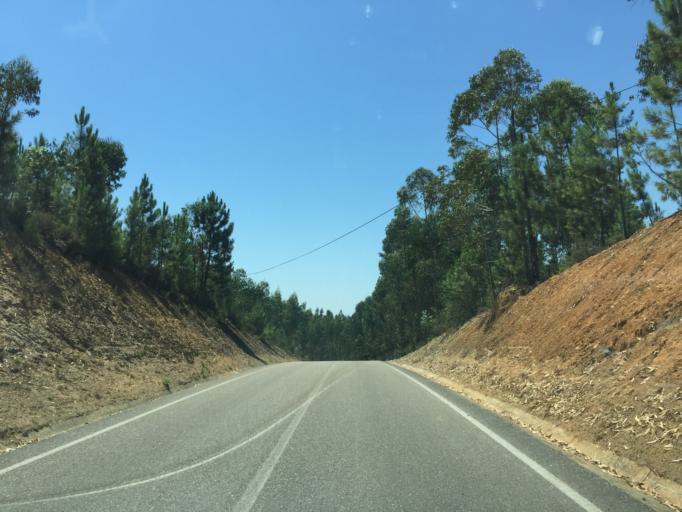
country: PT
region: Santarem
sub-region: Ferreira do Zezere
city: Ferreira do Zezere
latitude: 39.5910
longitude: -8.2989
